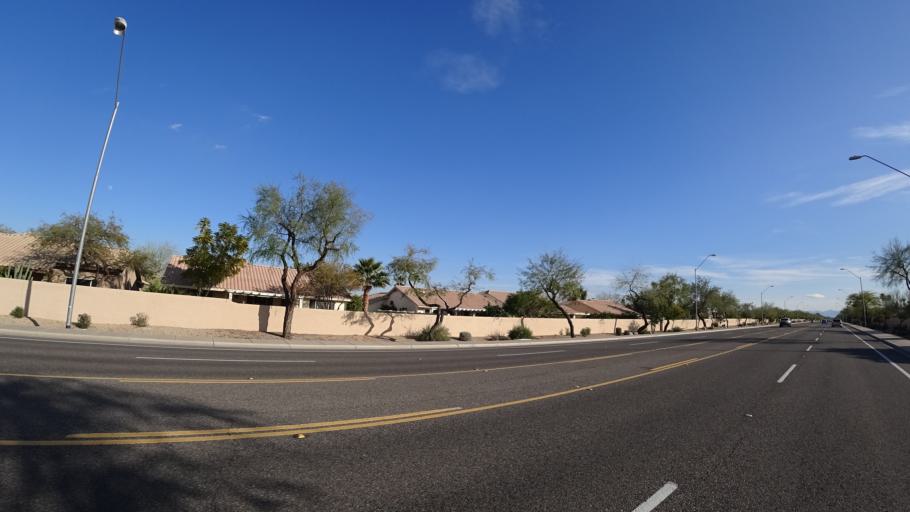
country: US
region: Arizona
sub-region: Maricopa County
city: Sun City
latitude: 33.6617
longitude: -112.2551
